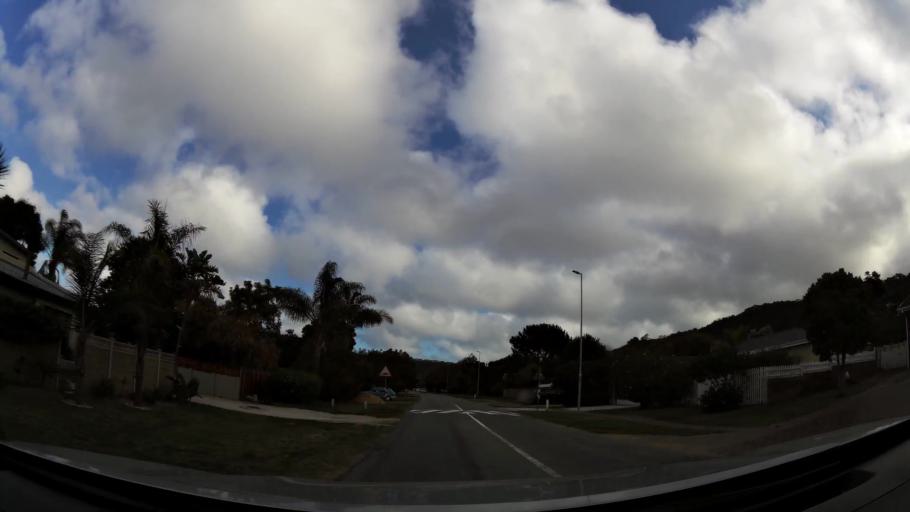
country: ZA
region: Western Cape
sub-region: Eden District Municipality
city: Plettenberg Bay
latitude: -34.0774
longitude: 23.3648
